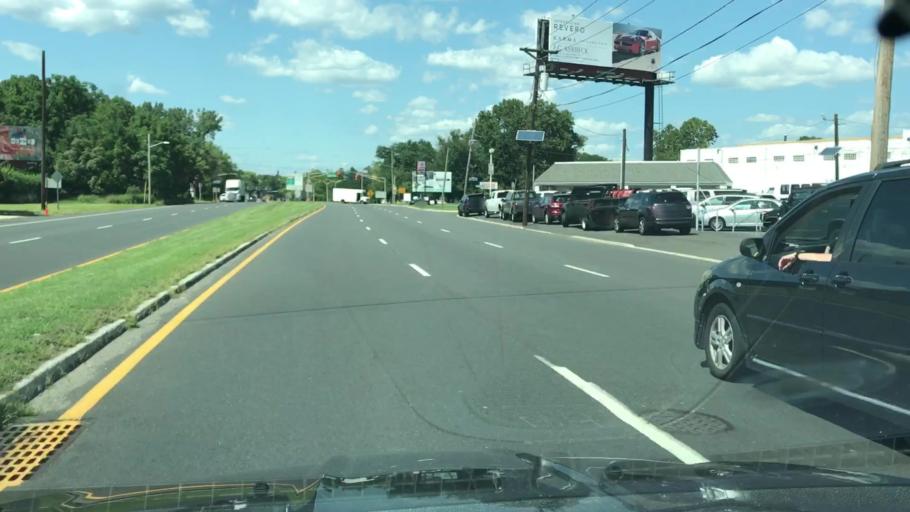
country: US
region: New Jersey
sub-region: Burlington County
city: Palmyra
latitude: 40.0030
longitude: -75.0369
